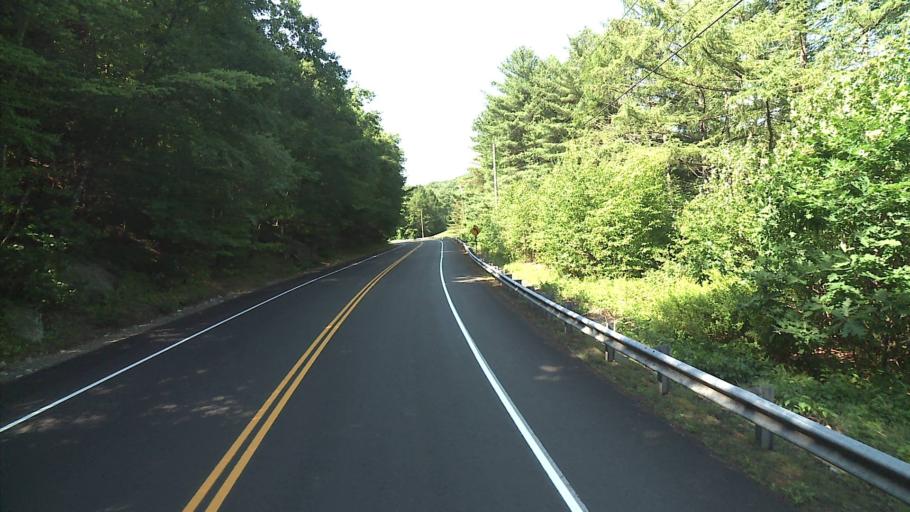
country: US
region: Connecticut
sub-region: Litchfield County
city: Terryville
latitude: 41.7428
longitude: -73.0172
